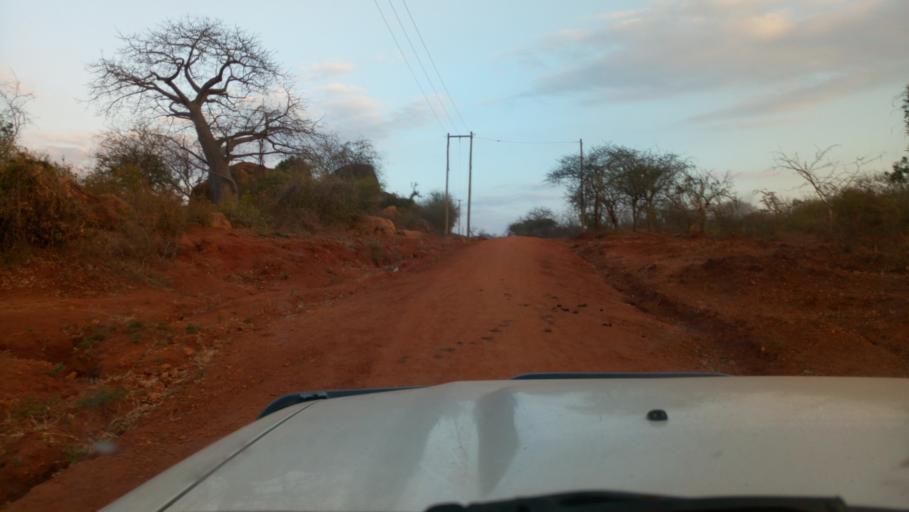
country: KE
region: Kitui
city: Kitui
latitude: -1.6928
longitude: 38.2335
